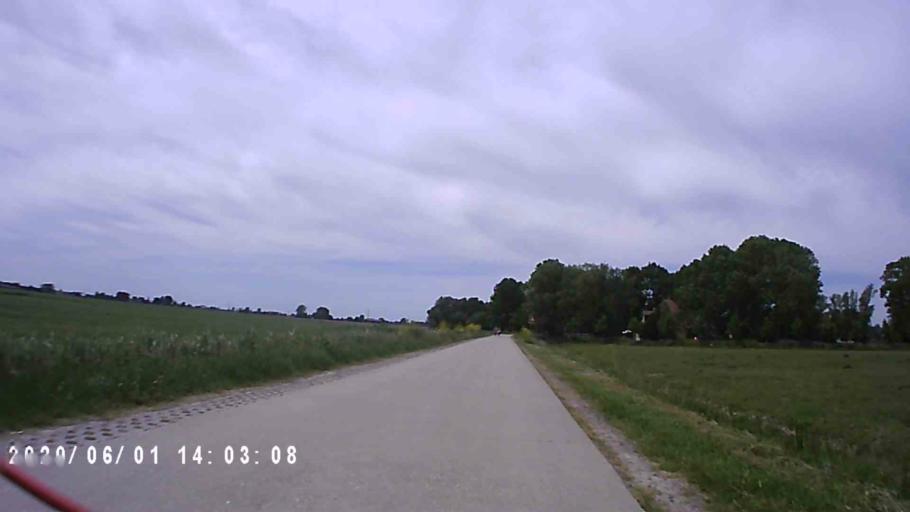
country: NL
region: Friesland
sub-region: Gemeente Littenseradiel
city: Winsum
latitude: 53.1119
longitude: 5.6380
